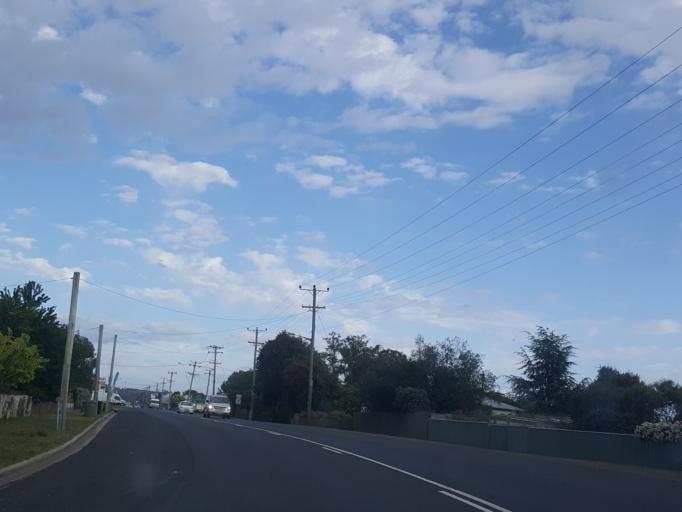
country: AU
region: Tasmania
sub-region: Northern Midlands
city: Perth
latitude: -41.5797
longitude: 147.1785
